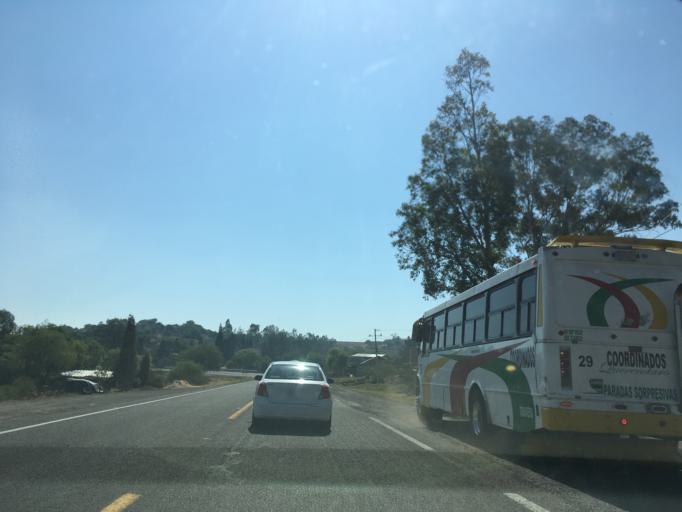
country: MX
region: Michoacan
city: Indaparapeo
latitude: 19.7848
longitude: -100.9916
